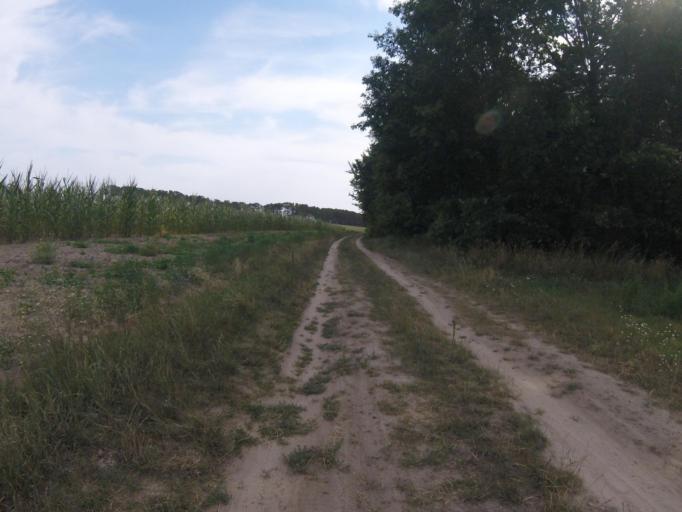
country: DE
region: Brandenburg
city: Wildau
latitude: 52.3095
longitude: 13.7227
